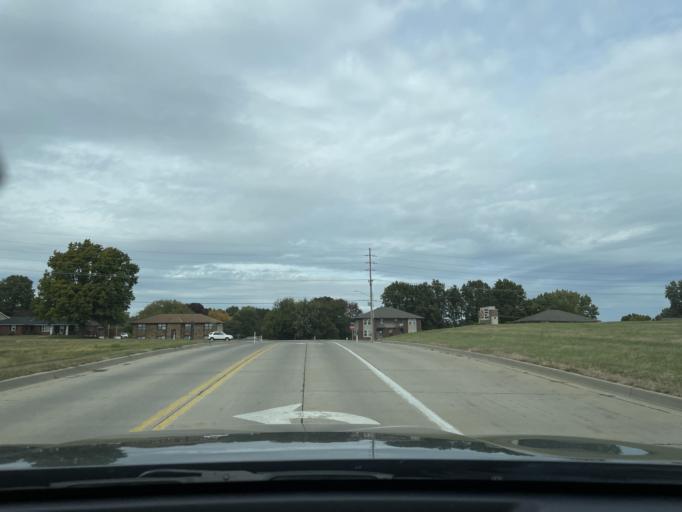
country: US
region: Missouri
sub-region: Buchanan County
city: Saint Joseph
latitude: 39.7690
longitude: -94.7811
